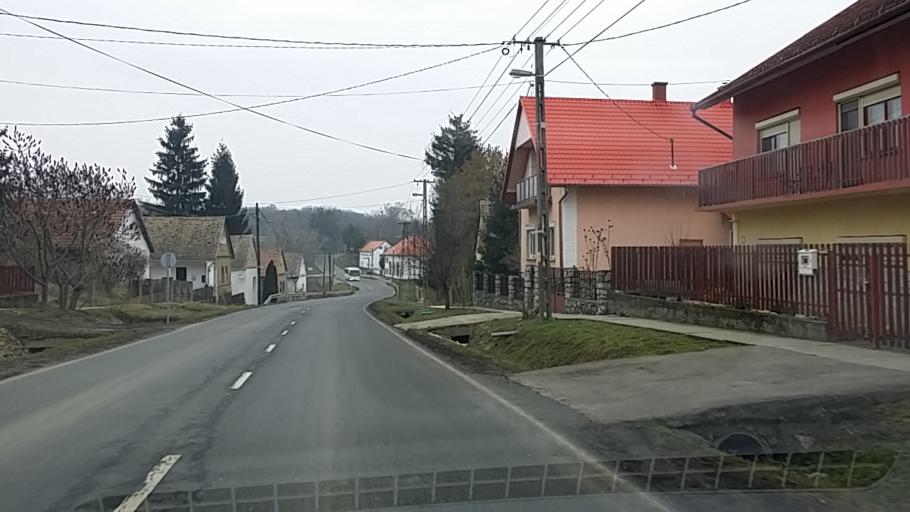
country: HU
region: Baranya
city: Dunaszekcso
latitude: 46.0527
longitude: 18.7179
